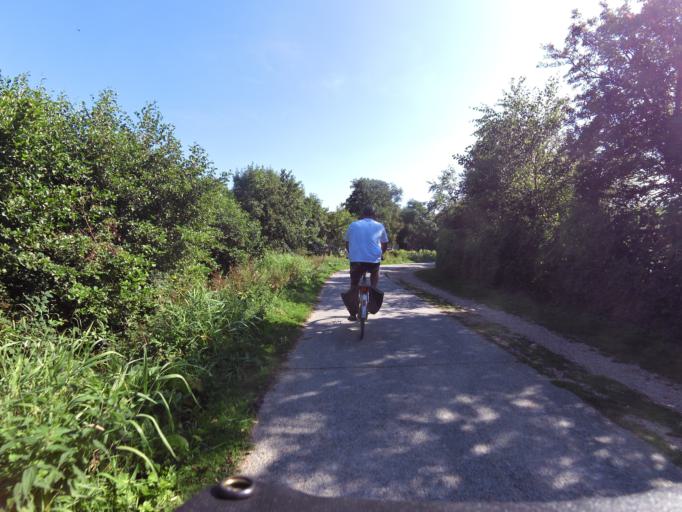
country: NL
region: Zeeland
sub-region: Schouwen-Duiveland
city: Haamstede
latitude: 51.7194
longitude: 3.7274
